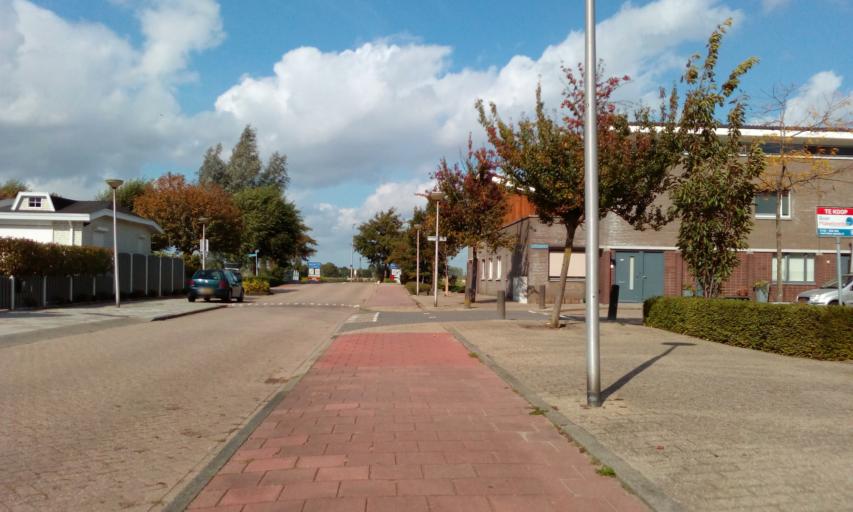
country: NL
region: South Holland
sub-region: Gemeente Gouda
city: Bloemendaal
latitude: 51.9925
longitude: 4.6647
